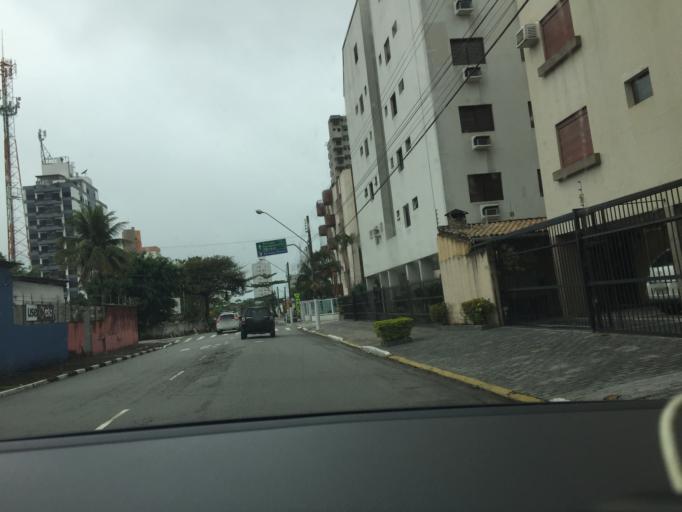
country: BR
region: Sao Paulo
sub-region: Guaruja
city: Guaruja
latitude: -23.9799
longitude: -46.2254
